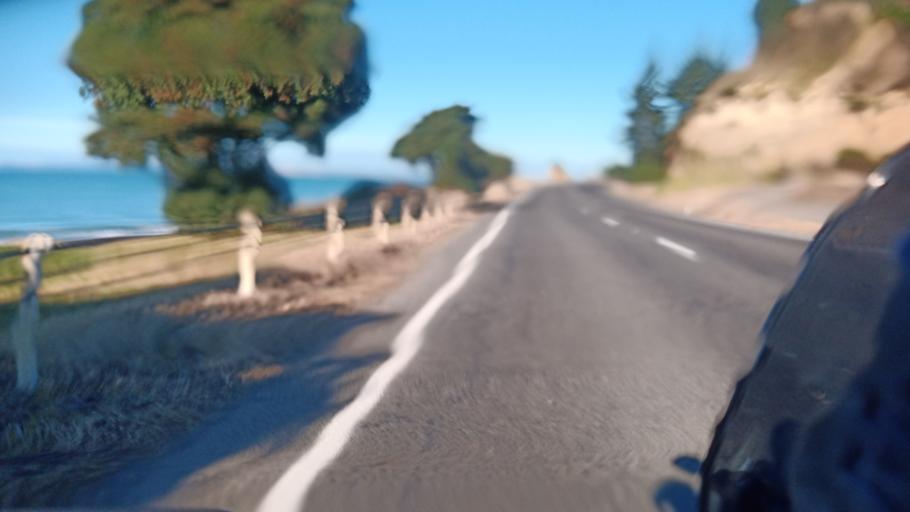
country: NZ
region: Hawke's Bay
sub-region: Napier City
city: Napier
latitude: -39.3625
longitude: 176.9025
